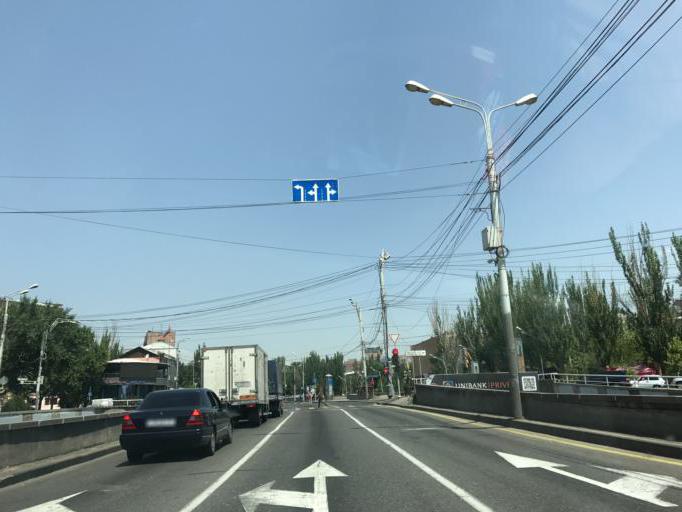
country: AM
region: Yerevan
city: Yerevan
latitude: 40.1791
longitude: 44.5234
